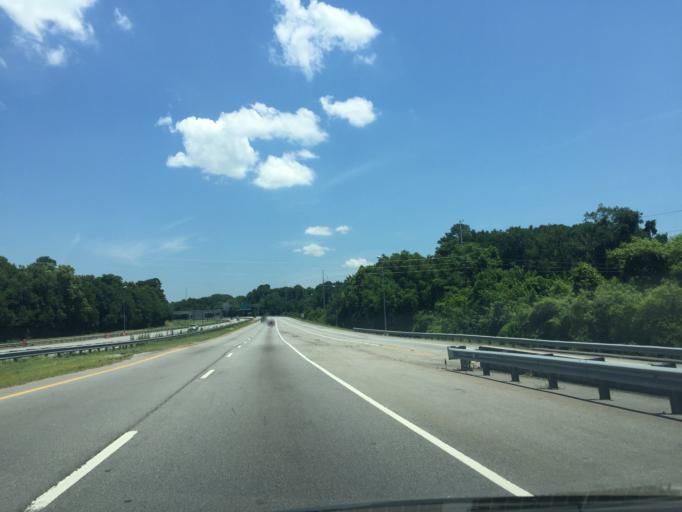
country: US
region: Georgia
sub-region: Chatham County
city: Thunderbolt
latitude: 32.0249
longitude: -81.0870
